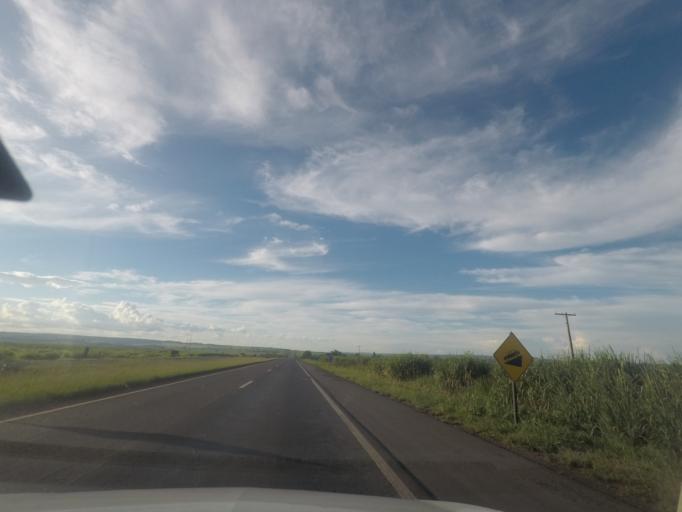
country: BR
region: Goias
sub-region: Itumbiara
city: Itumbiara
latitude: -18.2409
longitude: -49.2561
